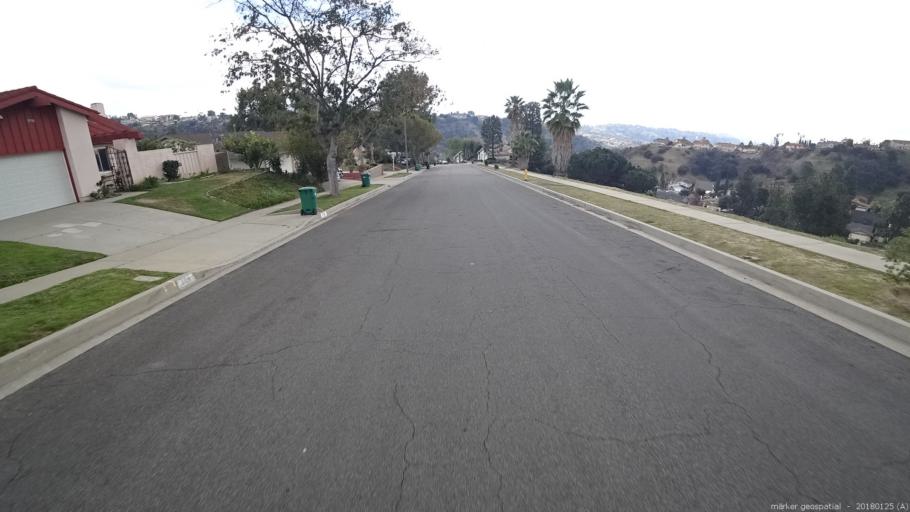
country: US
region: California
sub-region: Los Angeles County
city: Diamond Bar
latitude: 33.9912
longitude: -117.8261
